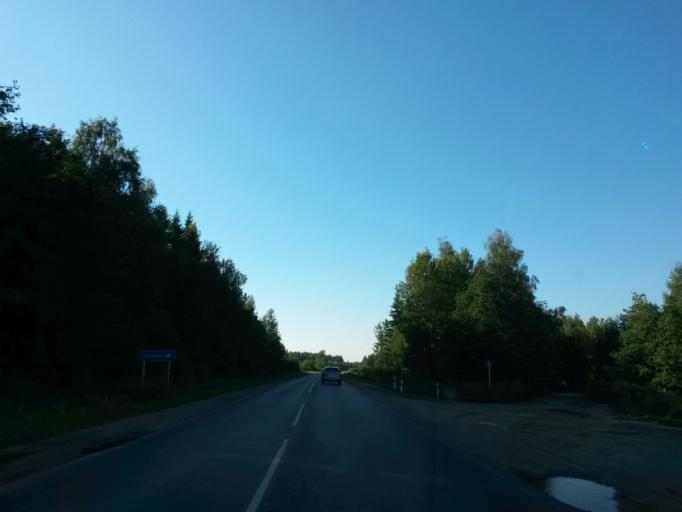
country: RU
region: Ivanovo
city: Novo-Talitsy
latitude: 57.0301
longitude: 40.7535
